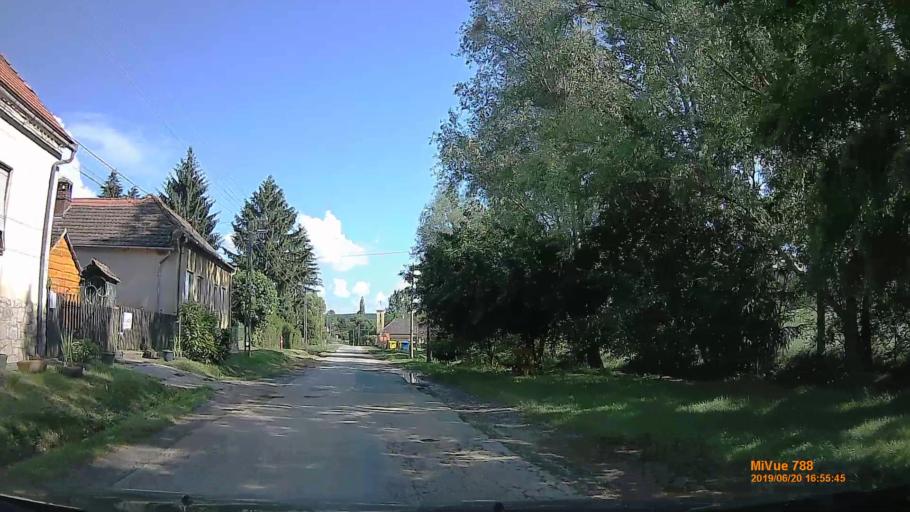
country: HU
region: Baranya
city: Buekkoesd
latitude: 46.1536
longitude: 18.0581
